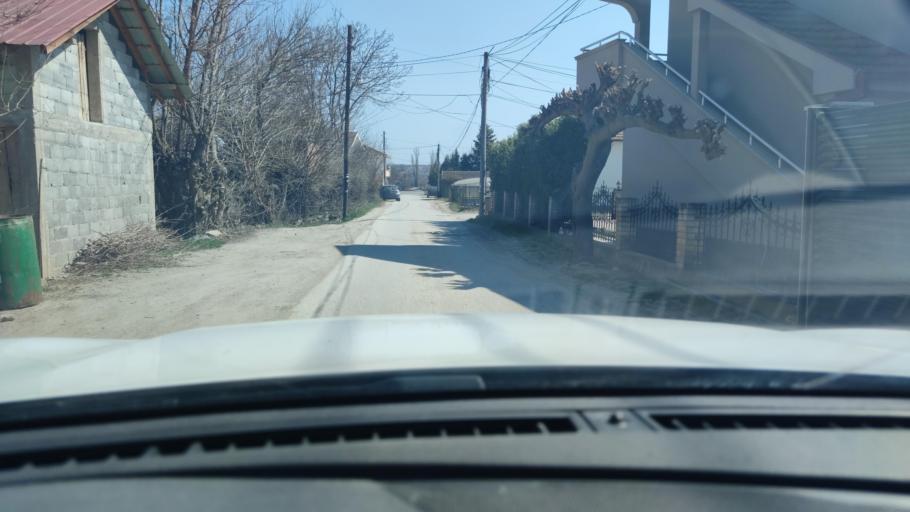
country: MK
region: Rosoman
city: Rosoman
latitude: 41.5199
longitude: 21.9430
